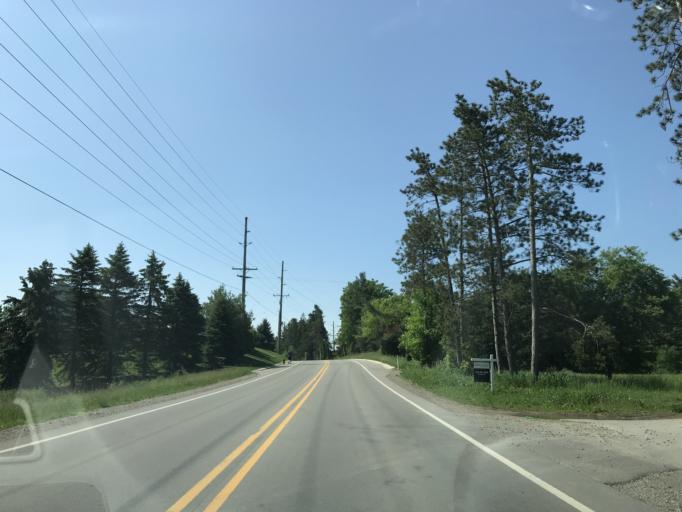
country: US
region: Michigan
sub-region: Oakland County
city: South Lyon
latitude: 42.4787
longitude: -83.6976
